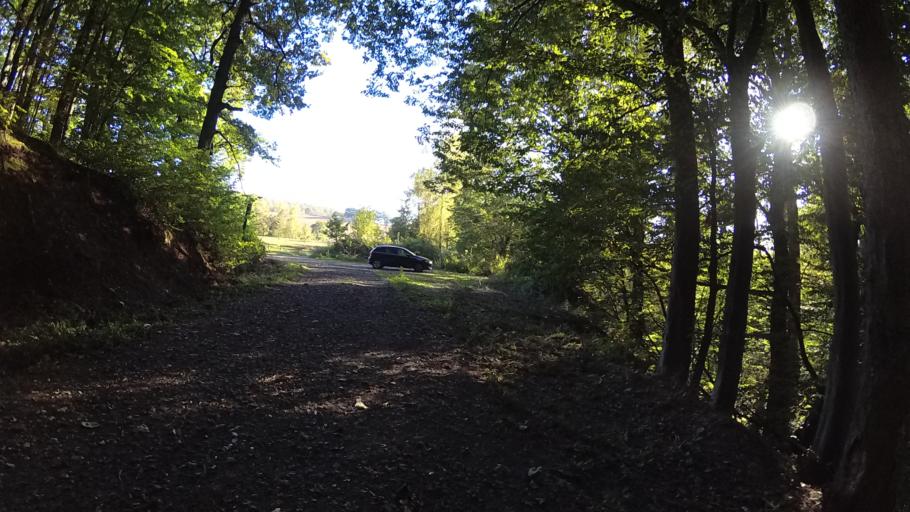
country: DE
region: Saarland
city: Sankt Wendel
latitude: 49.4337
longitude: 7.1794
